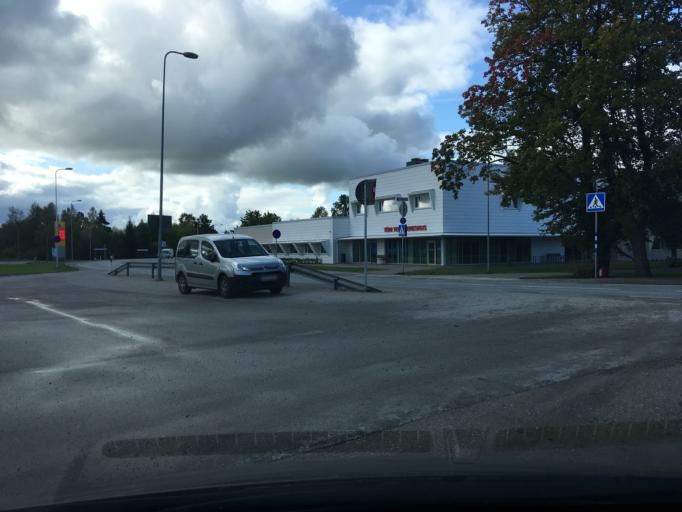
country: EE
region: Jaervamaa
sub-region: Tueri vald
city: Tueri
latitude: 58.8024
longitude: 25.4297
